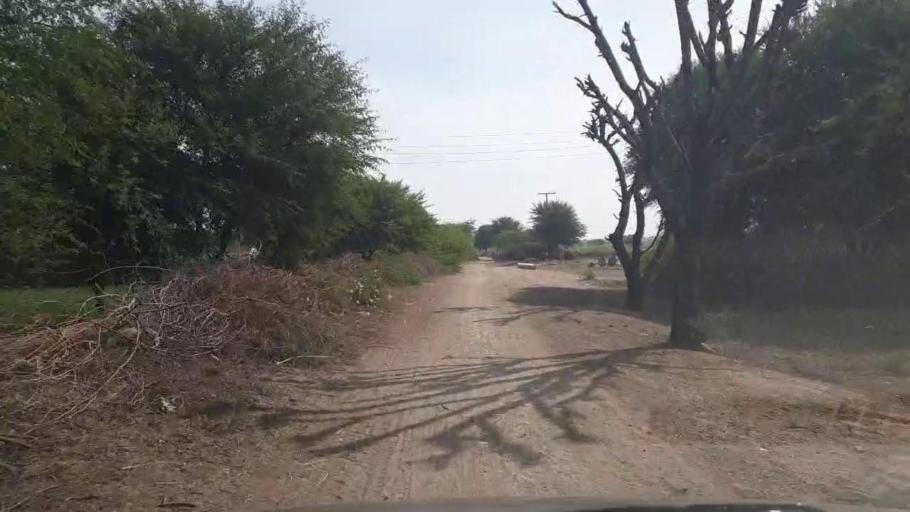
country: PK
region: Sindh
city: Umarkot
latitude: 25.2948
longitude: 69.7099
